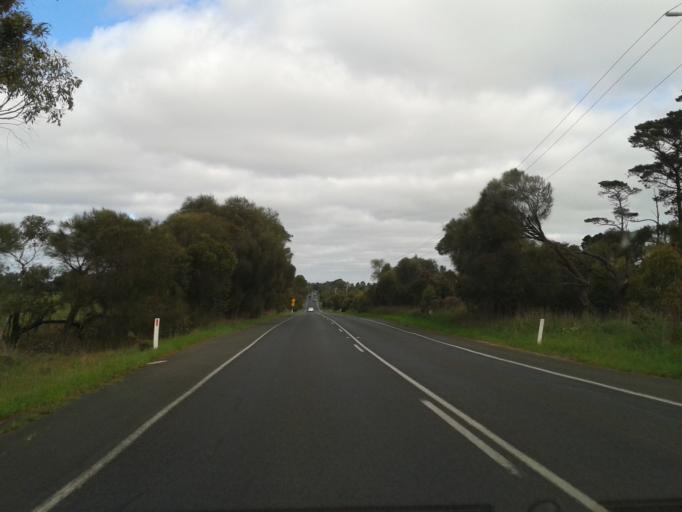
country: AU
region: Victoria
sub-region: Surf Coast
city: Anglesea
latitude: -38.3379
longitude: 144.2804
